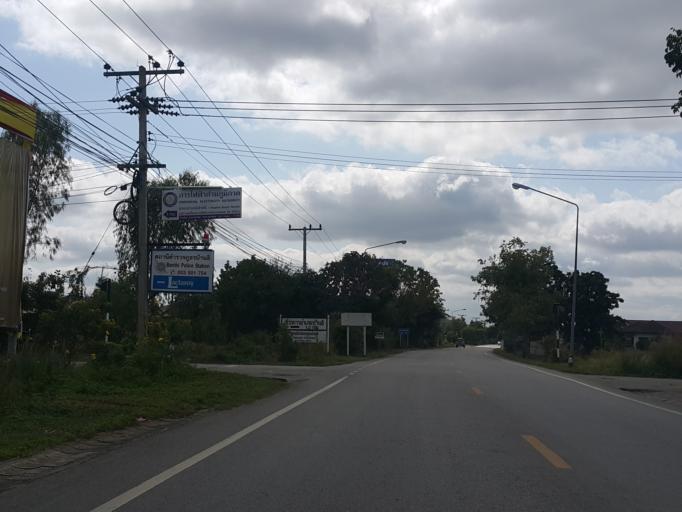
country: TH
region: Lamphun
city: Ban Thi
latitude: 18.6355
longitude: 99.1045
